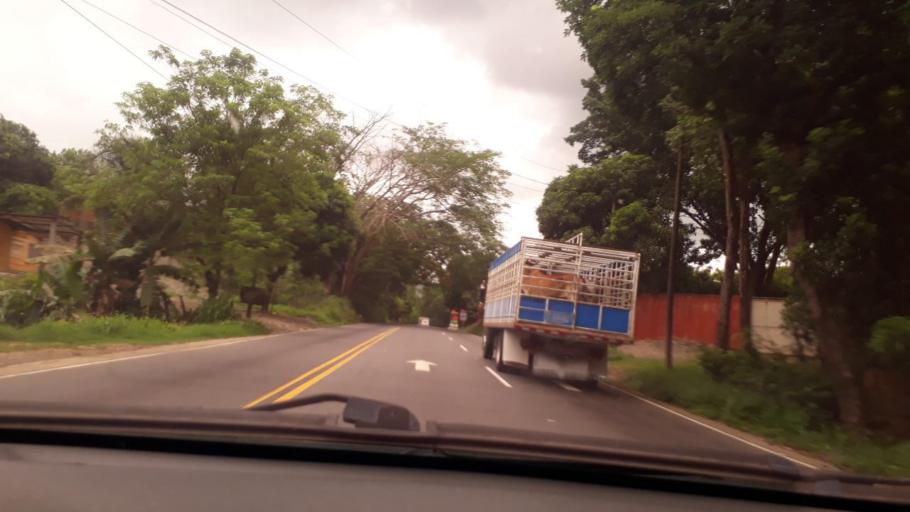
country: GT
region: Izabal
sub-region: Municipio de Los Amates
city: Los Amates
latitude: 15.2301
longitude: -89.2120
